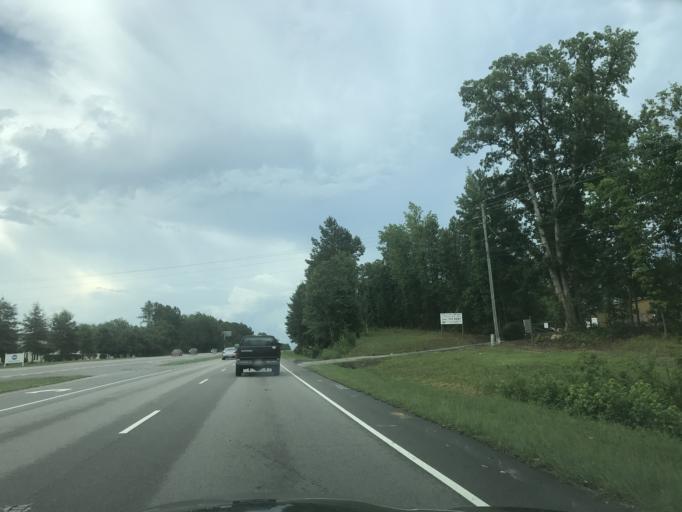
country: US
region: North Carolina
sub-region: Wake County
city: Garner
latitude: 35.6831
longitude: -78.5367
